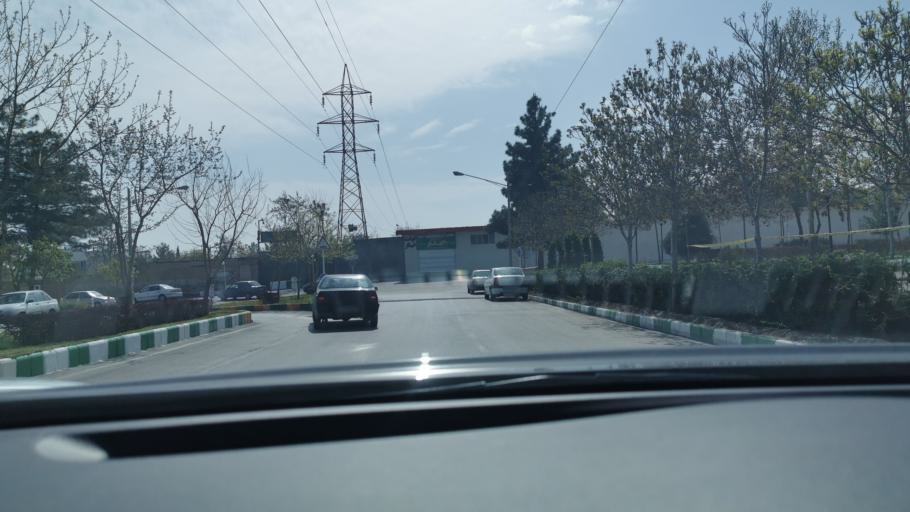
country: IR
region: Razavi Khorasan
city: Mashhad
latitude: 36.2806
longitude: 59.5486
